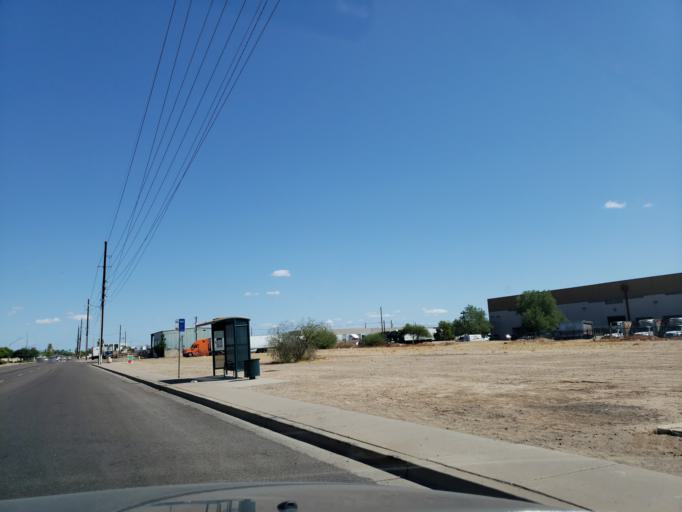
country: US
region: Arizona
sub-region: Maricopa County
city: Glendale
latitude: 33.5421
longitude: -112.2030
